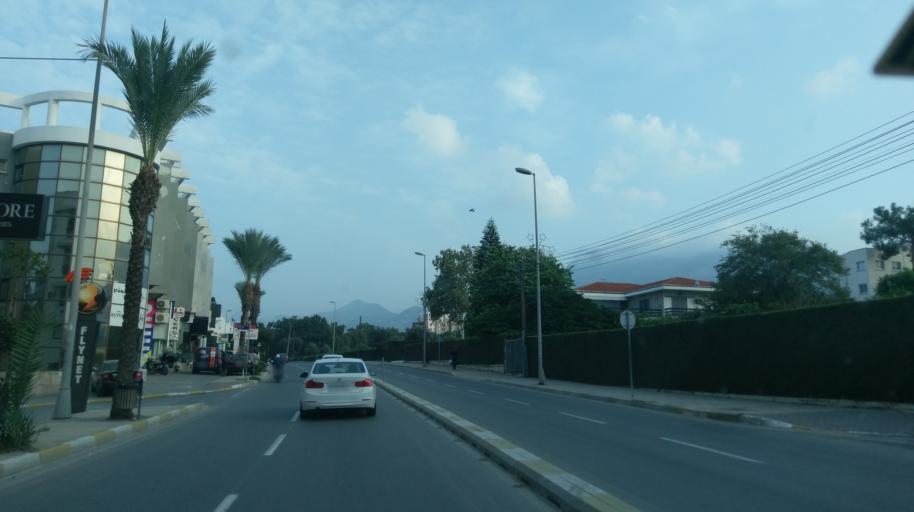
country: CY
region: Keryneia
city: Kyrenia
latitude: 35.3337
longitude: 33.3122
